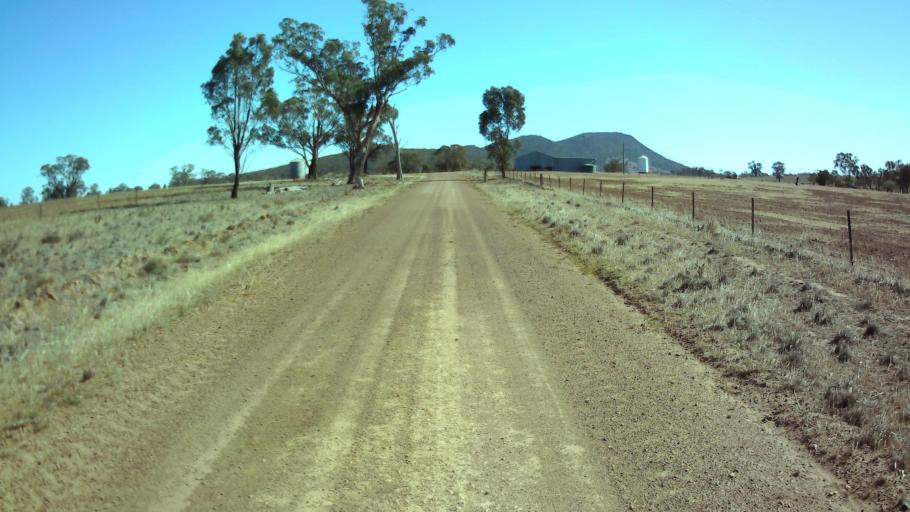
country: AU
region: New South Wales
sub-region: Weddin
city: Grenfell
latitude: -33.7702
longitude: 147.9231
